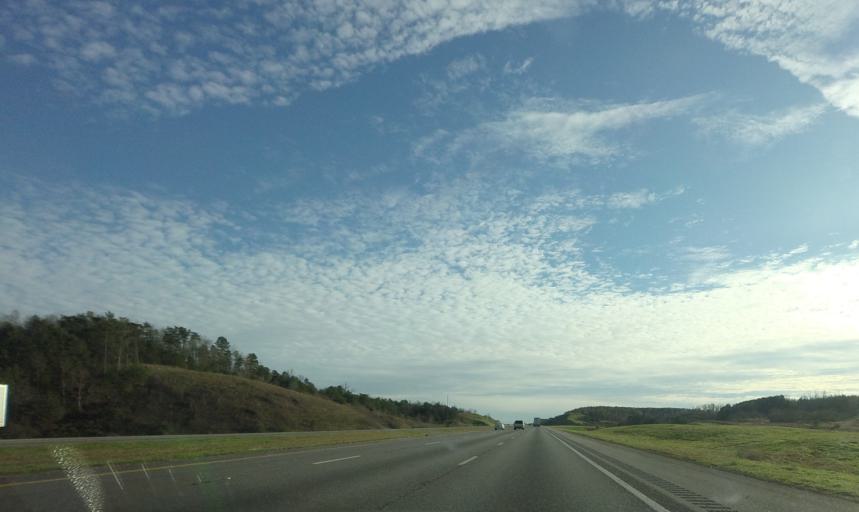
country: US
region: Alabama
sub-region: Walker County
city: Cordova
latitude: 33.7724
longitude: -87.2085
